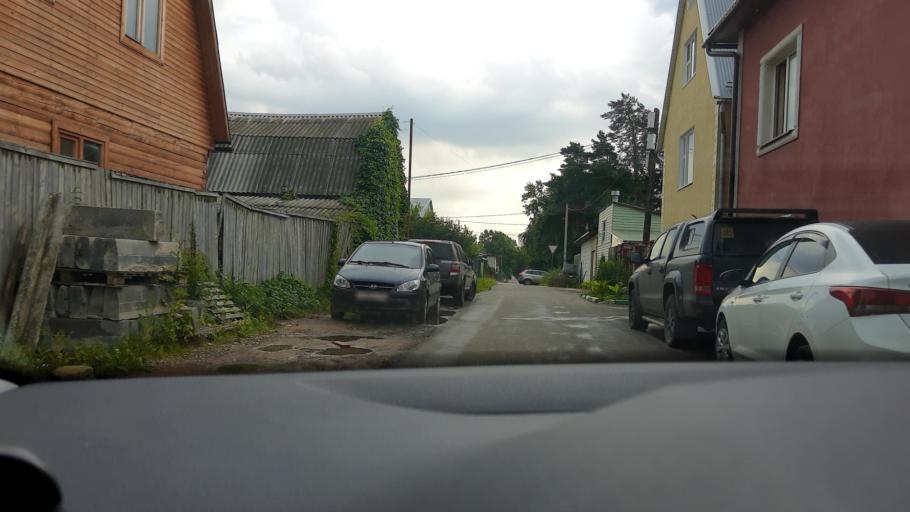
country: RU
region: Moskovskaya
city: Dolgoprudnyy
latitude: 55.9223
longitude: 37.4718
